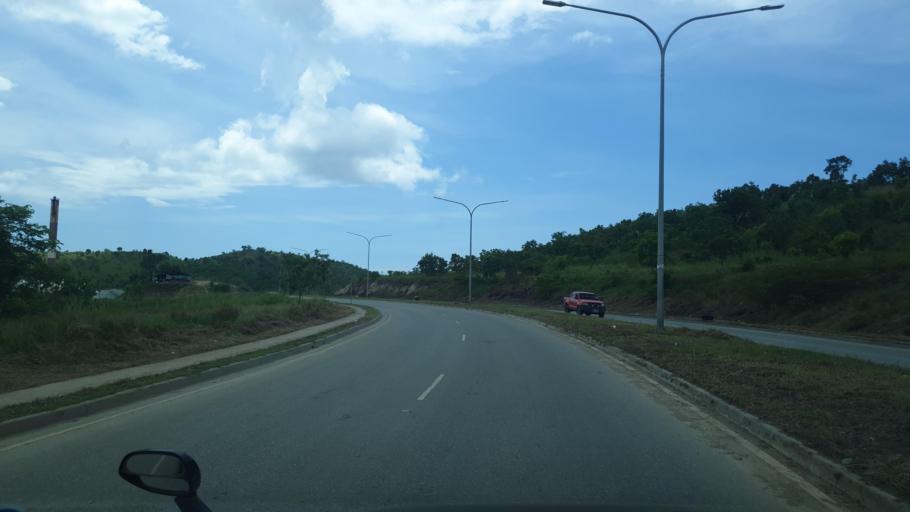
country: PG
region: National Capital
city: Port Moresby
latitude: -9.4280
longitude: 147.1408
